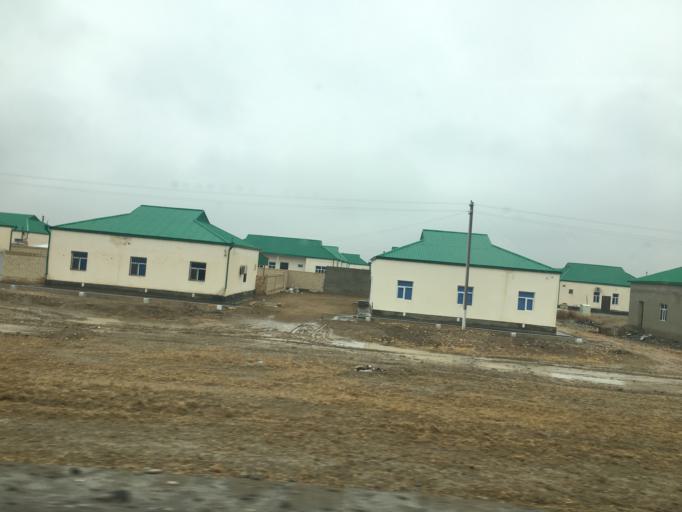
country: TM
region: Mary
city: Yoloeten
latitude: 37.2936
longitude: 62.3356
